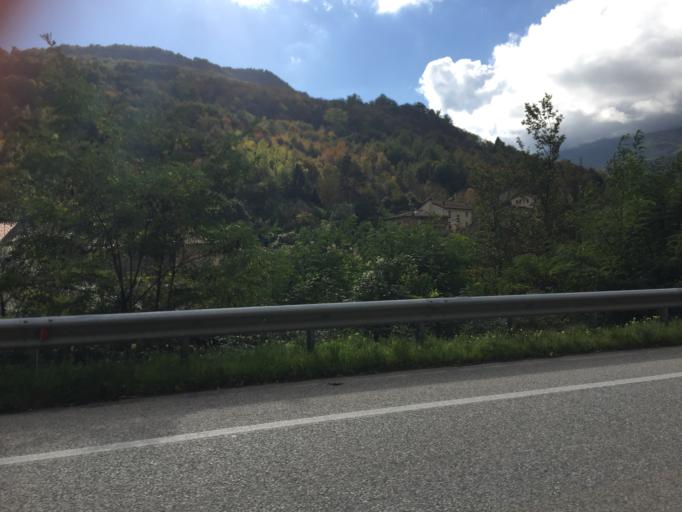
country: IT
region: The Marches
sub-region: Provincia di Ascoli Piceno
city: Arquata del Tronto
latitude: 42.7741
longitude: 13.3138
